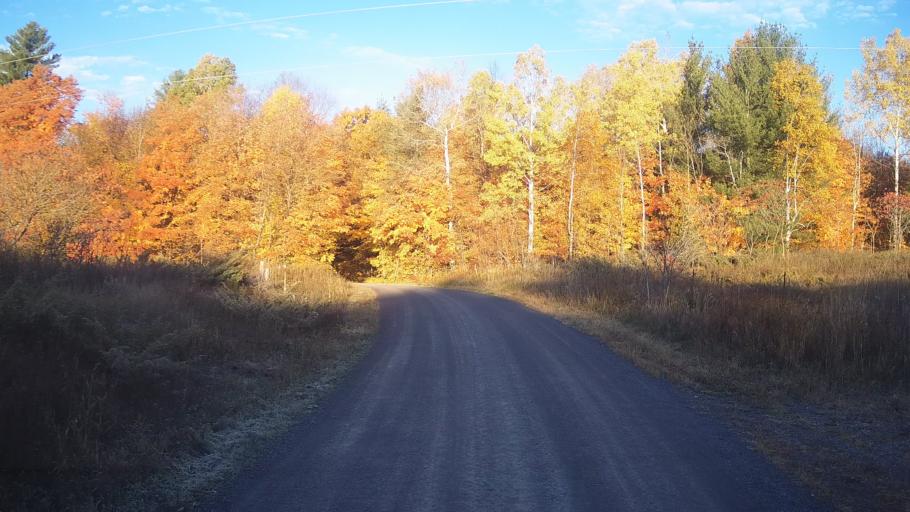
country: CA
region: Ontario
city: Arnprior
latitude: 45.3360
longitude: -76.3576
